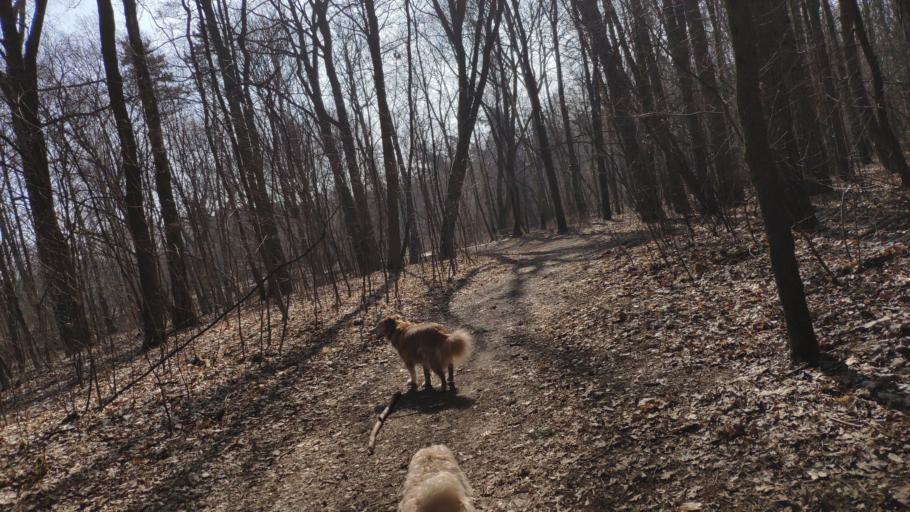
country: PL
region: Lodz Voivodeship
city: Lodz
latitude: 51.7697
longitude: 19.4043
